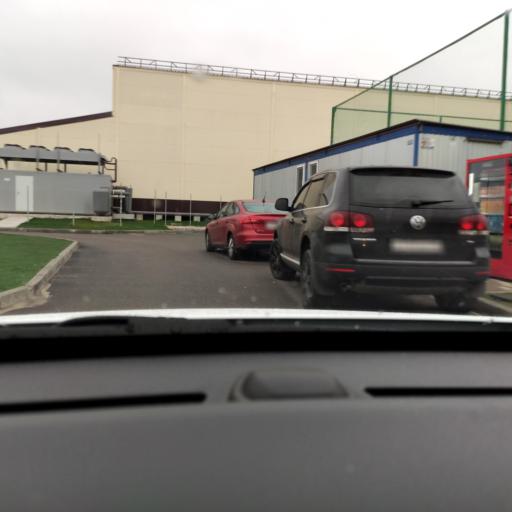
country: RU
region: Voronezj
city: Voronezh
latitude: 51.6738
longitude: 39.2380
